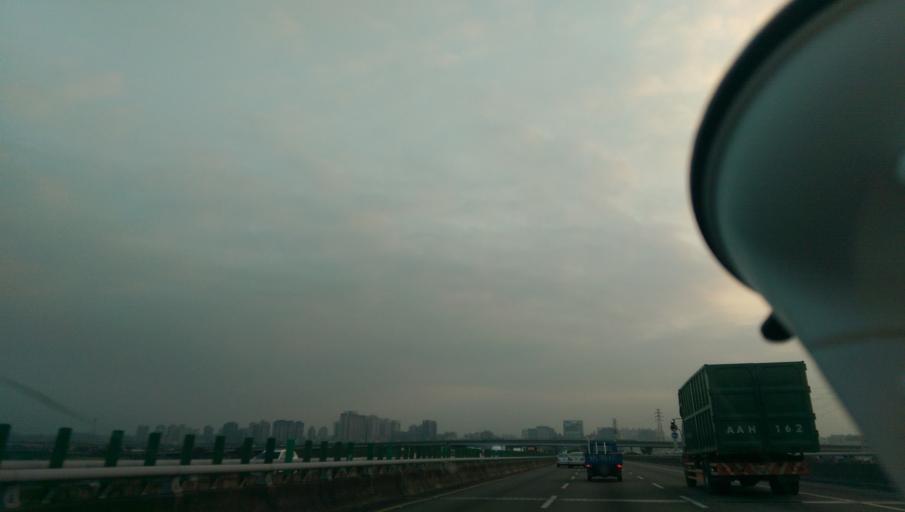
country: TW
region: Taiwan
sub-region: Hsinchu
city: Zhubei
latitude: 24.8150
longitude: 121.0123
